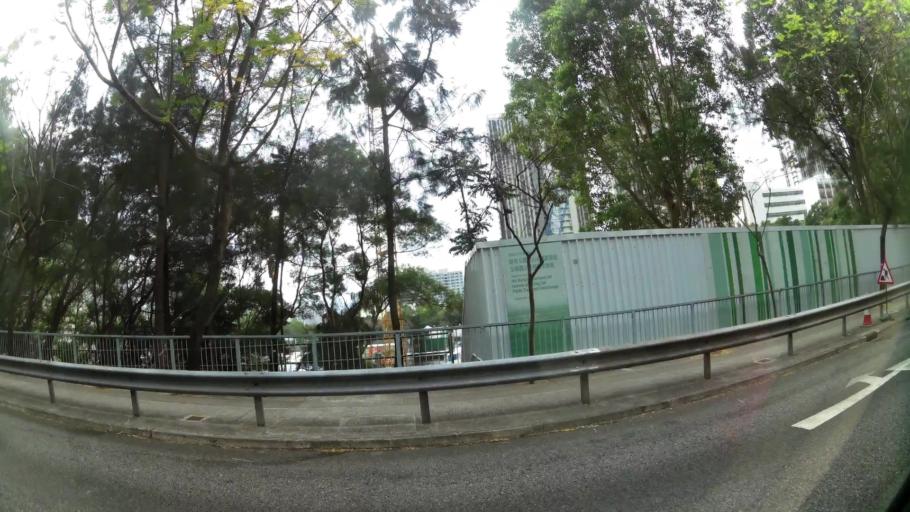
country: HK
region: Wong Tai Sin
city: Wong Tai Sin
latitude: 22.3450
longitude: 114.1881
